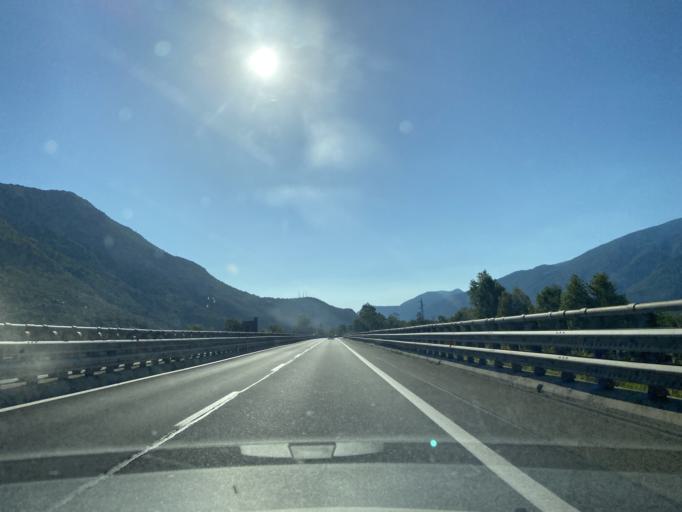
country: IT
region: Piedmont
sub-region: Provincia di Torino
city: Borgone Susa
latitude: 45.1230
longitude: 7.2262
